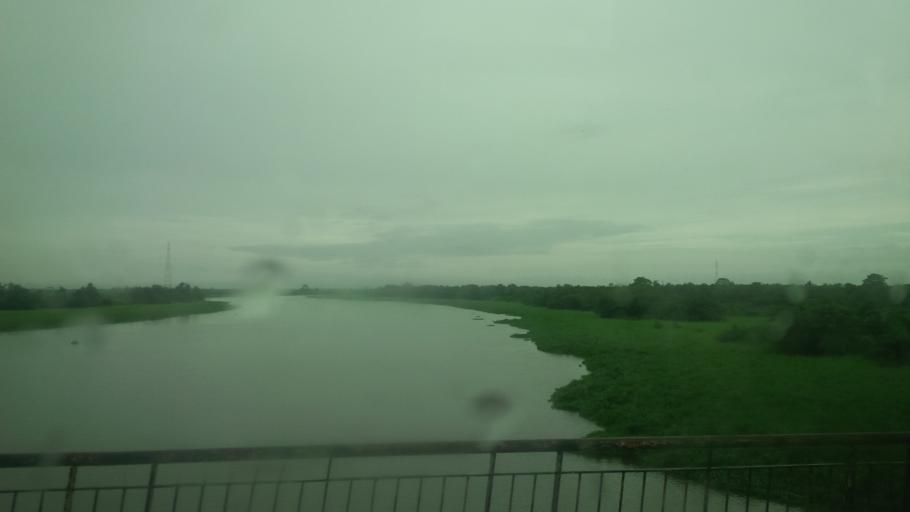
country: CI
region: Sud-Comoe
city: Grand-Bassam
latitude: 5.2161
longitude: -3.7153
